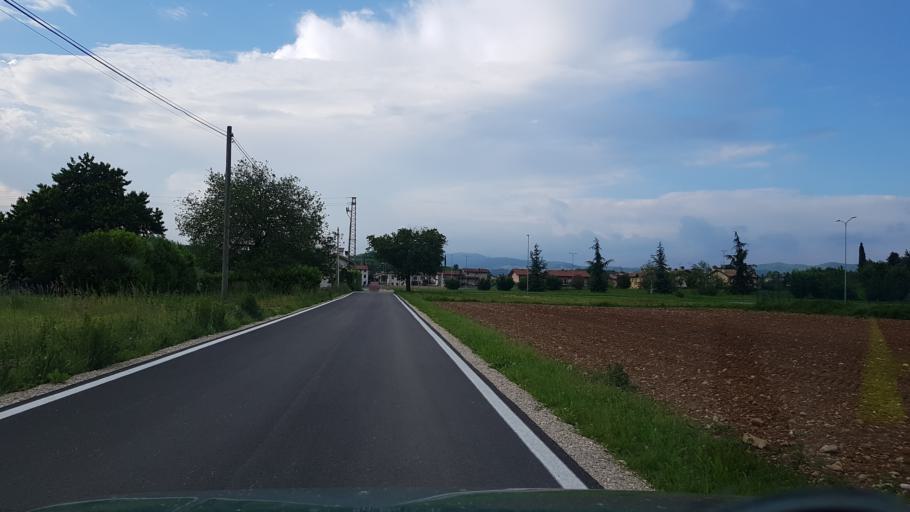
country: IT
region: Friuli Venezia Giulia
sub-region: Provincia di Gorizia
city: Mossa
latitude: 45.9311
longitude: 13.5426
